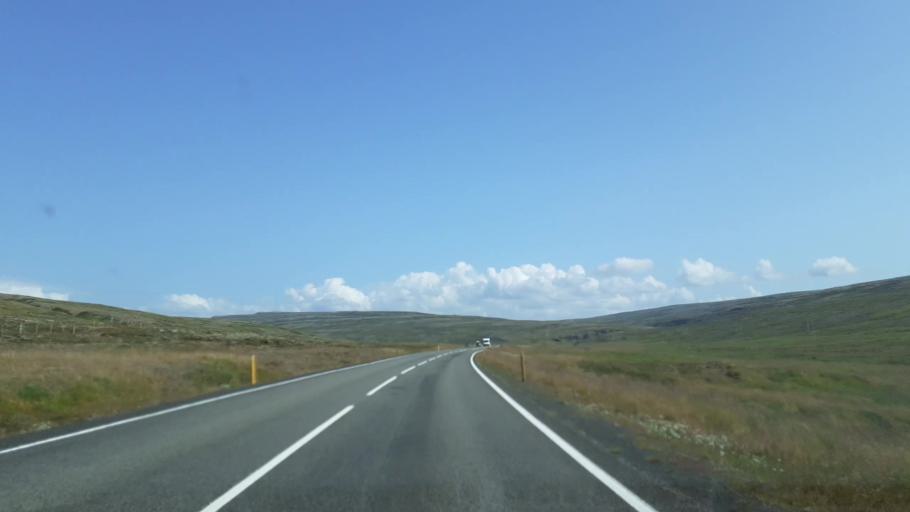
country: IS
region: West
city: Borgarnes
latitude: 64.8472
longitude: -21.2418
